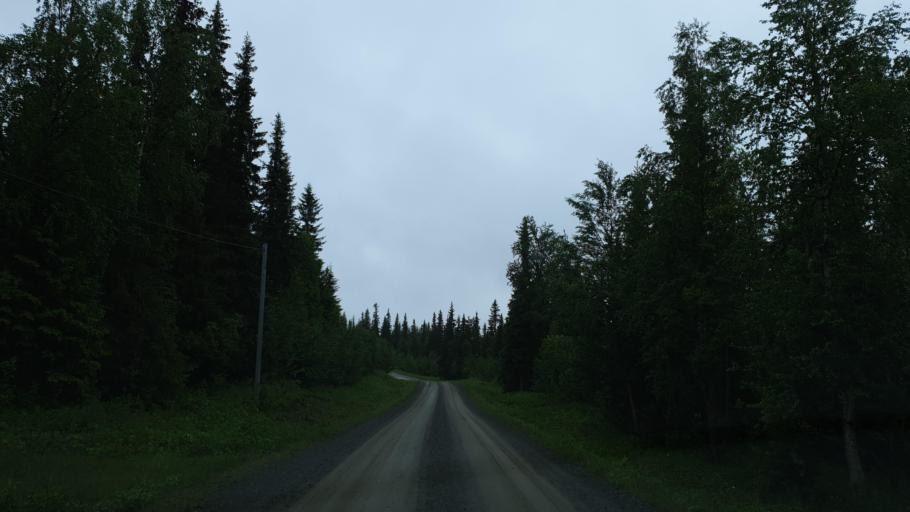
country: SE
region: Vaesterbotten
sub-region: Vilhelmina Kommun
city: Sjoberg
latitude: 65.3341
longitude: 15.9007
